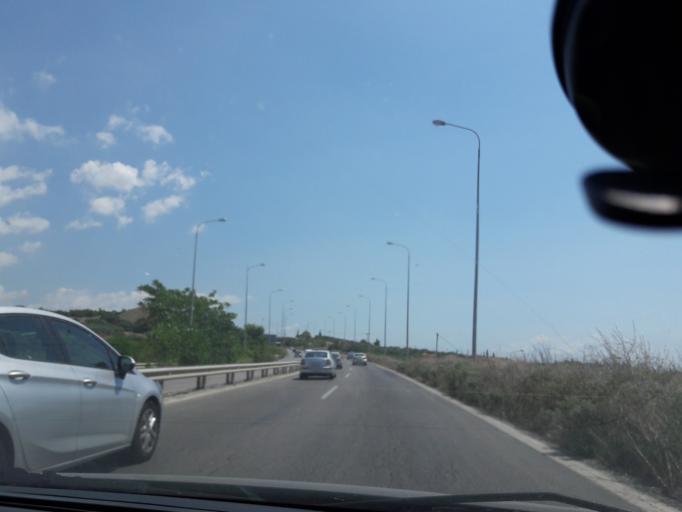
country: GR
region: Central Macedonia
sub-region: Nomos Chalkidikis
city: Nea Kallikrateia
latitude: 40.3141
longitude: 23.0953
